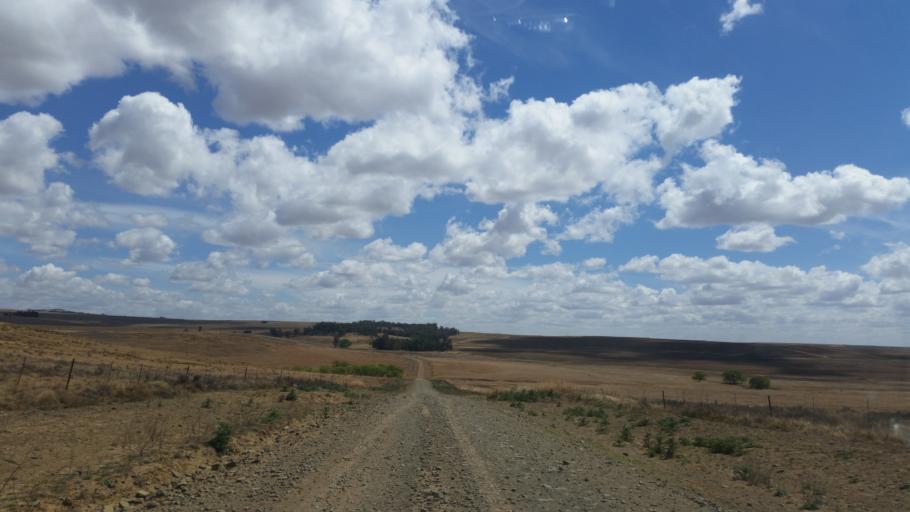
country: ZA
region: Orange Free State
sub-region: Thabo Mofutsanyana District Municipality
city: Bethlehem
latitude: -28.1916
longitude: 28.5943
